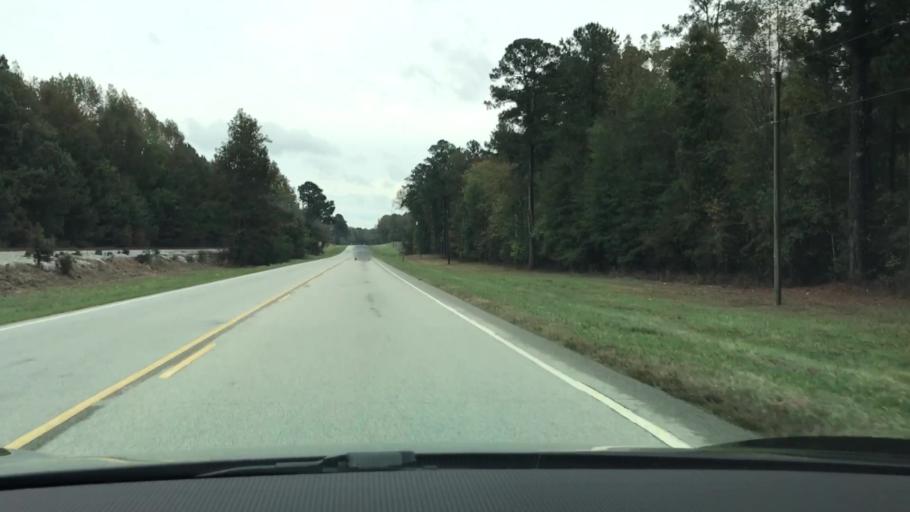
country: US
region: Georgia
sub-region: Warren County
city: Firing Range
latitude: 33.4728
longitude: -82.7244
